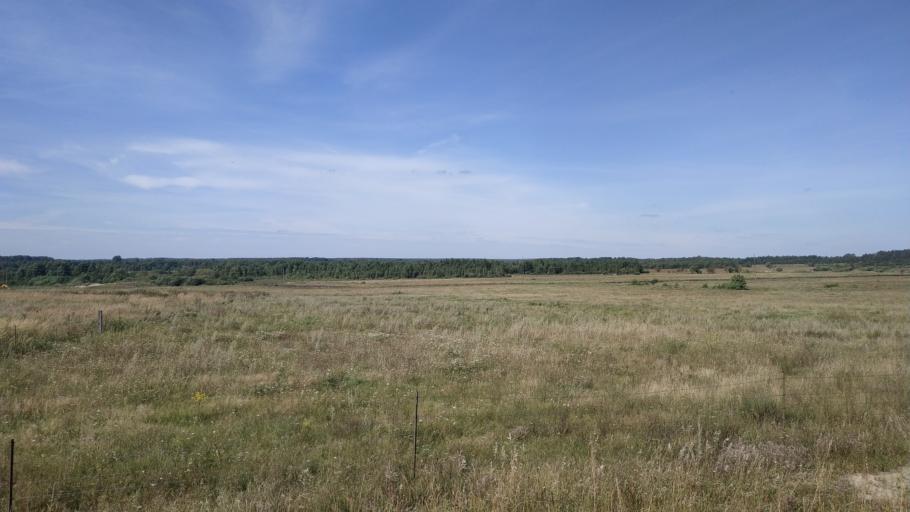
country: RU
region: Brjansk
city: Zhukovka
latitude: 53.5899
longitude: 33.8164
